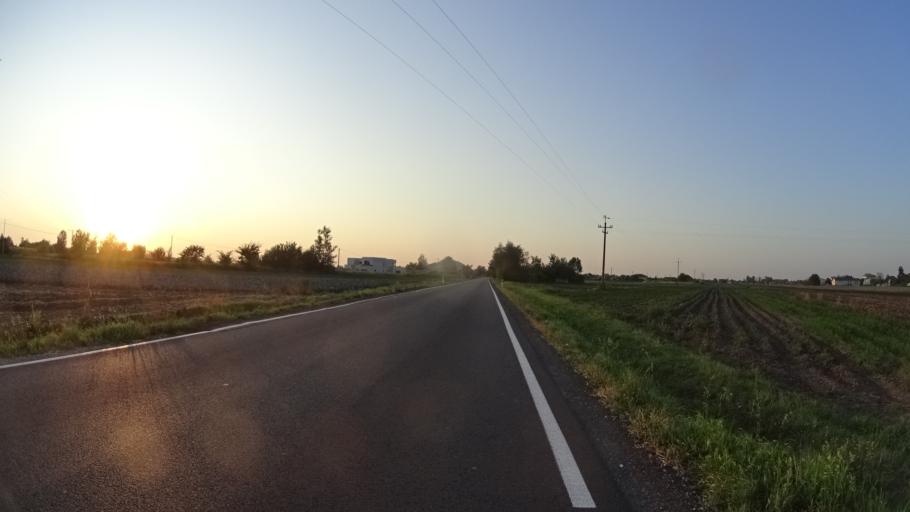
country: PL
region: Masovian Voivodeship
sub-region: Powiat warszawski zachodni
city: Ozarow Mazowiecki
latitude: 52.2416
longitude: 20.7502
